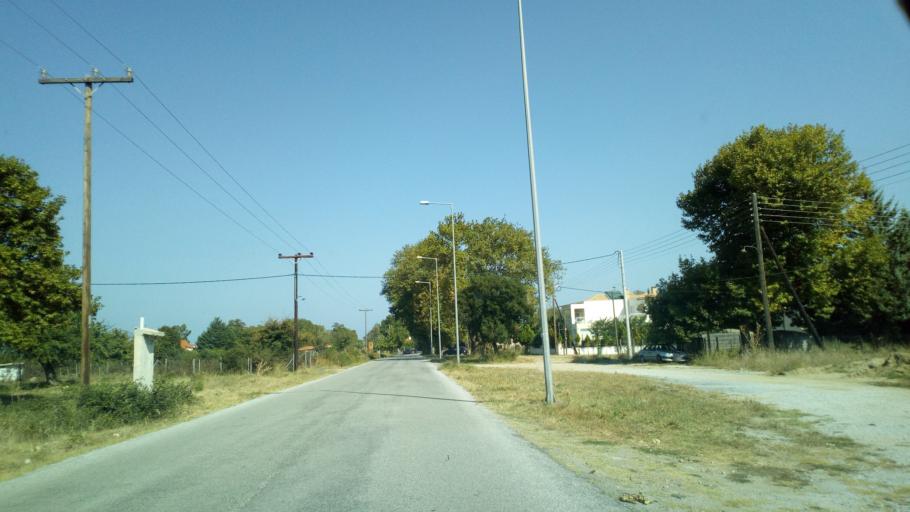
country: GR
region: Central Macedonia
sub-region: Nomos Chalkidikis
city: Stratonion
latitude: 40.5946
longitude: 23.7727
